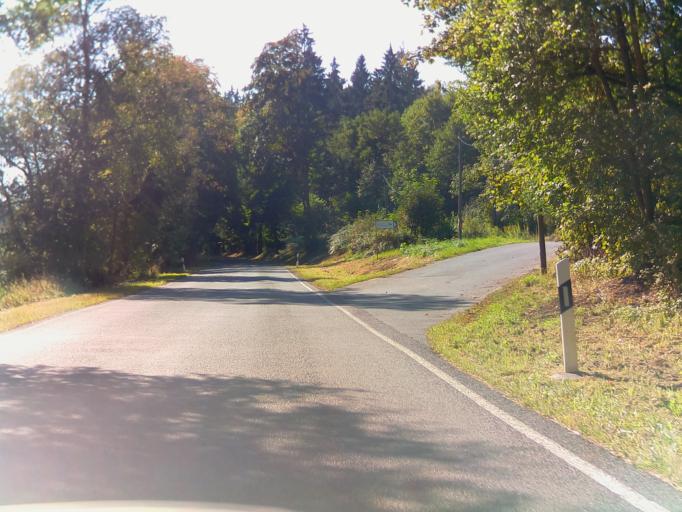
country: DE
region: Thuringia
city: Wurzbach
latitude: 50.4829
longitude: 11.4721
